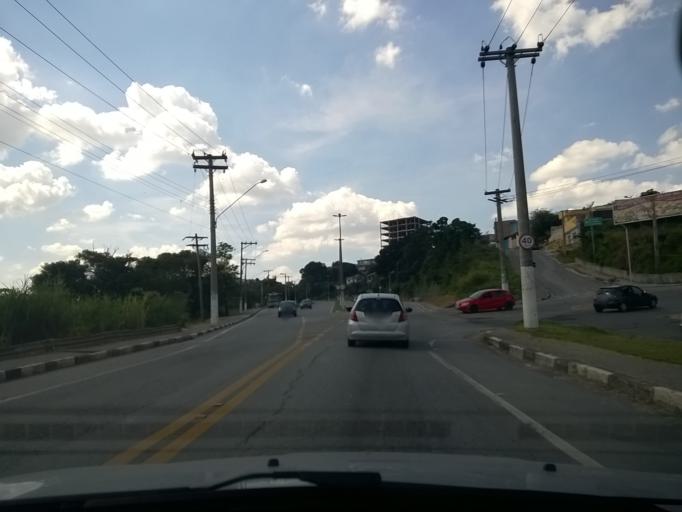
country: BR
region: Sao Paulo
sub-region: Francisco Morato
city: Francisco Morato
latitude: -23.2893
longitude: -46.7512
